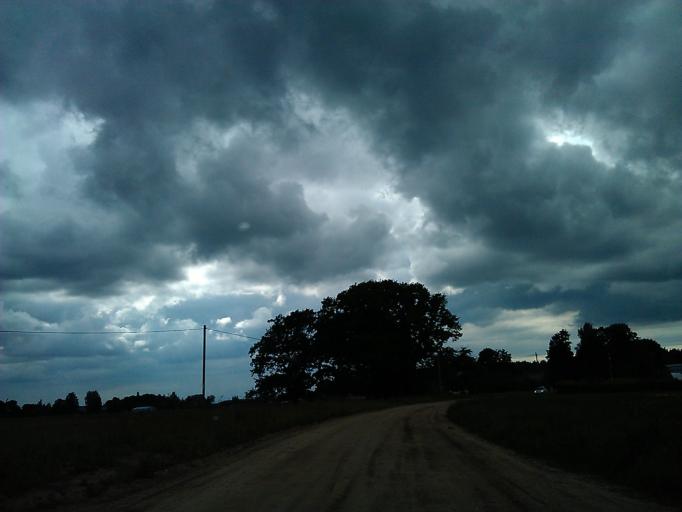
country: LV
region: Adazi
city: Adazi
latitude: 57.0842
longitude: 24.3033
